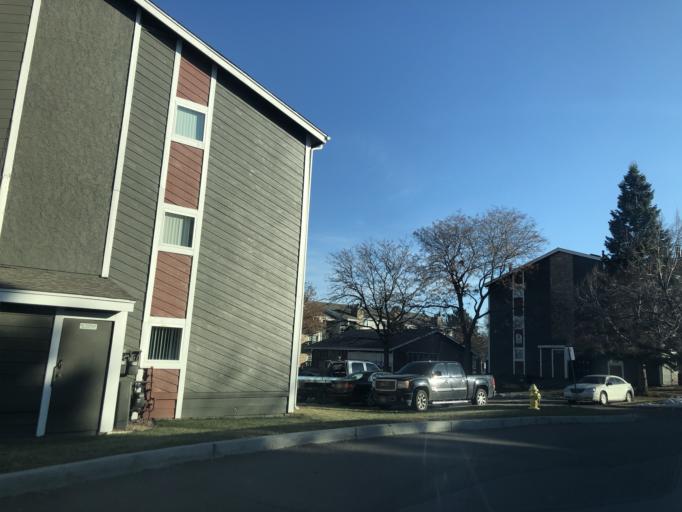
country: US
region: Colorado
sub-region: Adams County
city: Aurora
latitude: 39.7029
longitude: -104.8087
